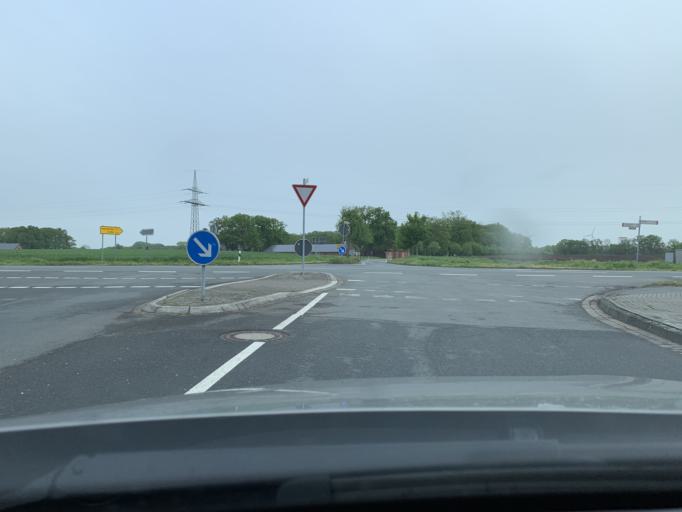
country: DE
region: North Rhine-Westphalia
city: Rietberg
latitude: 51.8042
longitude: 8.3807
